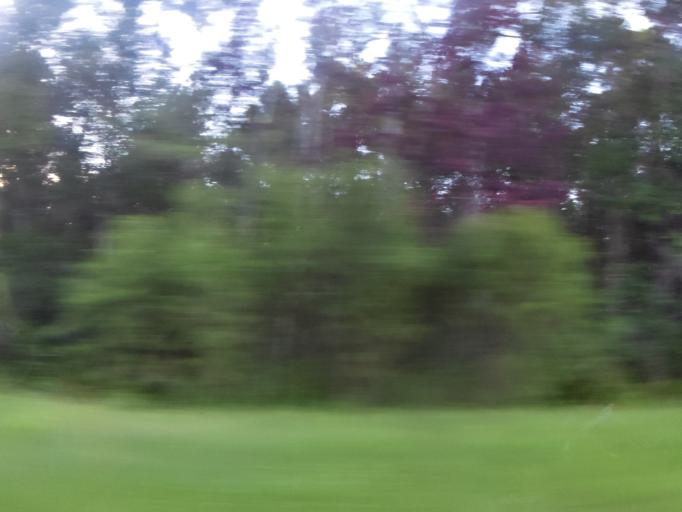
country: US
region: Georgia
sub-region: Camden County
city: Kings Bay Base
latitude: 30.7858
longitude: -81.6060
